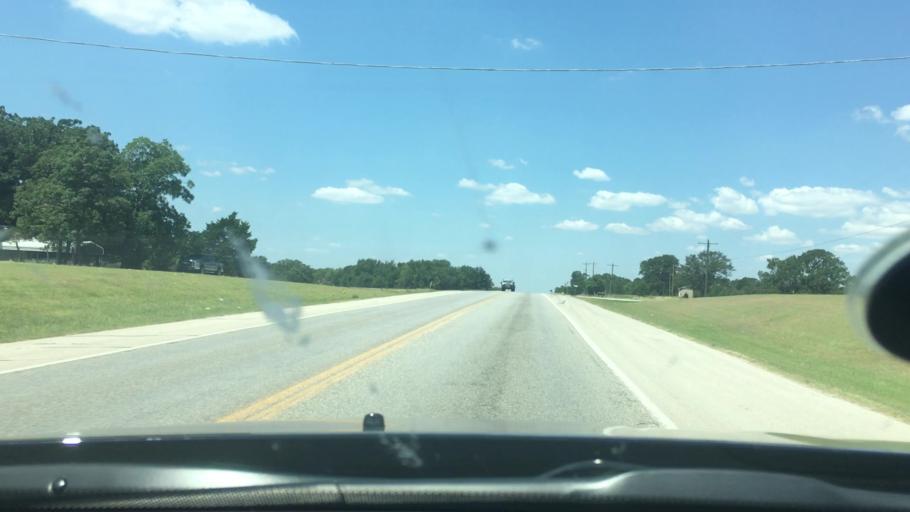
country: US
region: Oklahoma
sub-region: Carter County
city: Dickson
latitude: 34.1873
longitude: -96.9085
